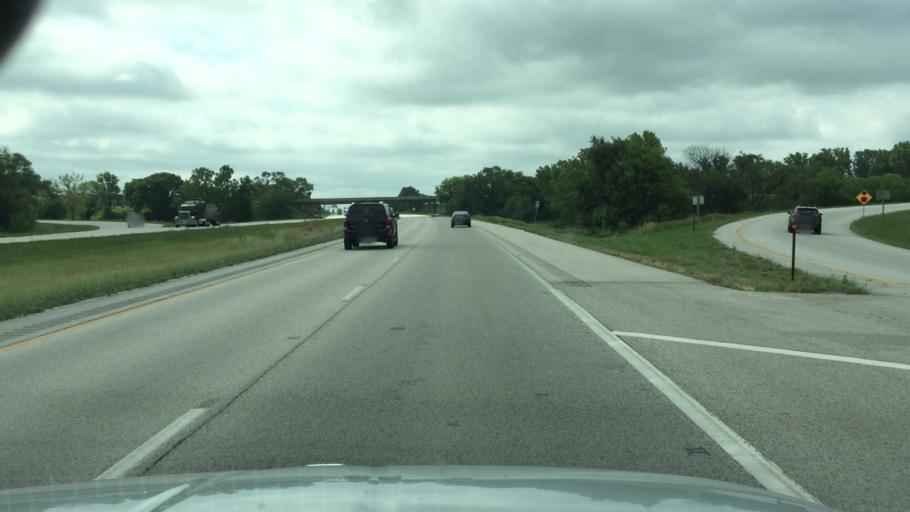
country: US
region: Illinois
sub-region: Henry County
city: Green Rock
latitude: 41.4575
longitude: -90.3379
